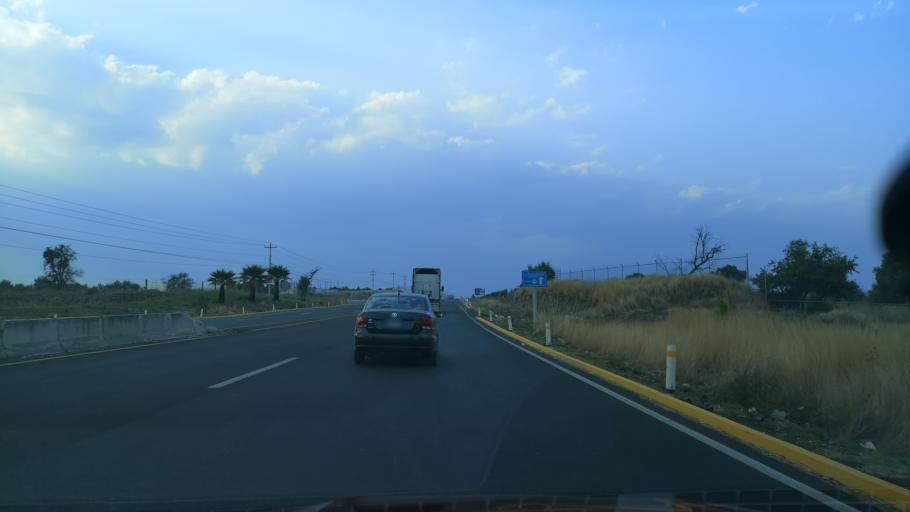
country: MX
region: Puebla
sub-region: Juan C. Bonilla
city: Santa Maria Zacatepec
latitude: 19.1353
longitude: -98.3736
